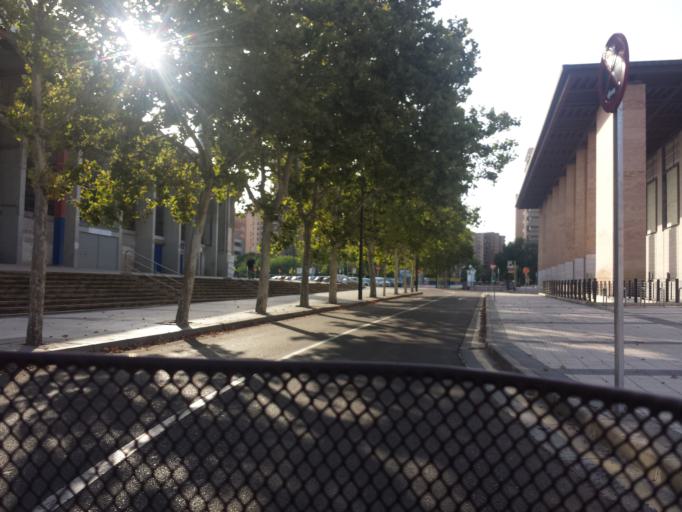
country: ES
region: Aragon
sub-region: Provincia de Zaragoza
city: Delicias
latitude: 41.6372
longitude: -0.9007
